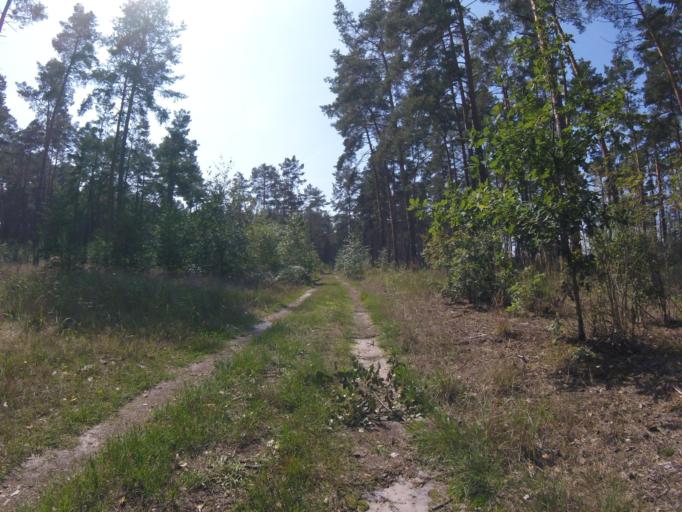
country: DE
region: Brandenburg
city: Bestensee
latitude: 52.2226
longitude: 13.6978
